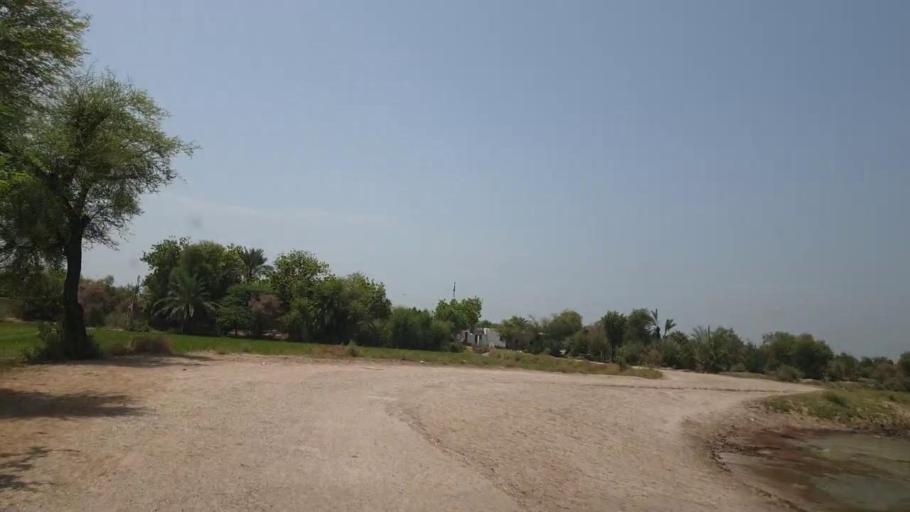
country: PK
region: Sindh
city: Lakhi
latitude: 27.8610
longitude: 68.6043
